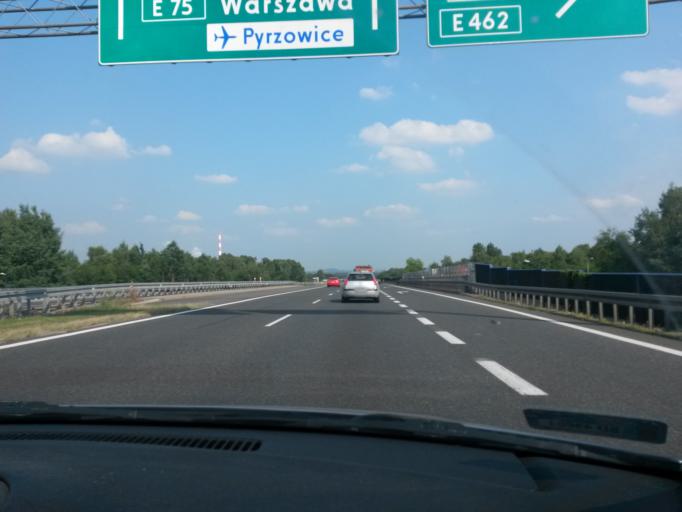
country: PL
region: Silesian Voivodeship
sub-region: Myslowice
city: Myslowice
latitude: 50.2099
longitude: 19.1571
